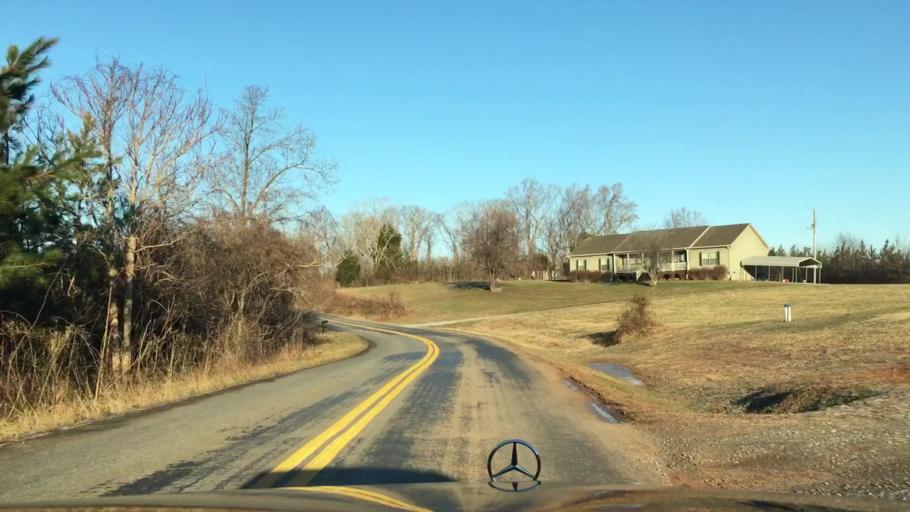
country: US
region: Virginia
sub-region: Pittsylvania County
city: Hurt
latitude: 37.1119
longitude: -79.3127
